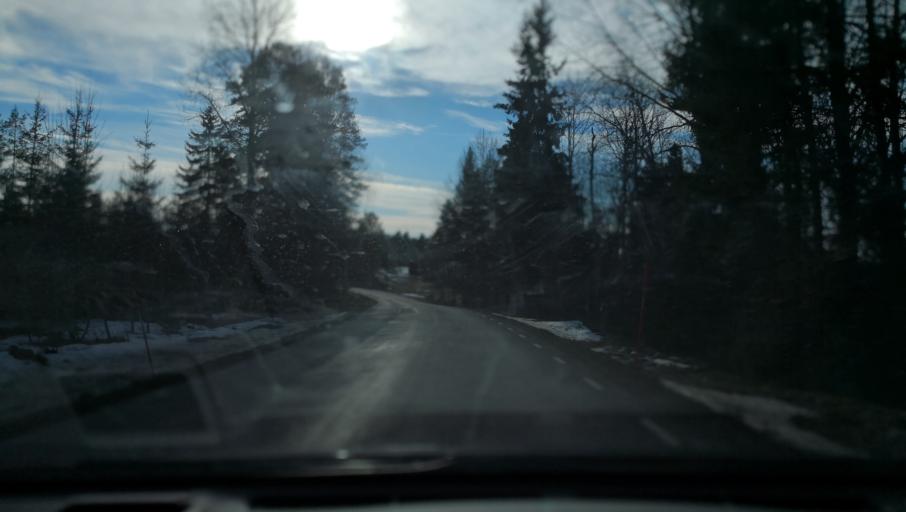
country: SE
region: Uppsala
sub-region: Osthammars Kommun
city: Osterbybruk
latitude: 60.2514
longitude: 17.9446
